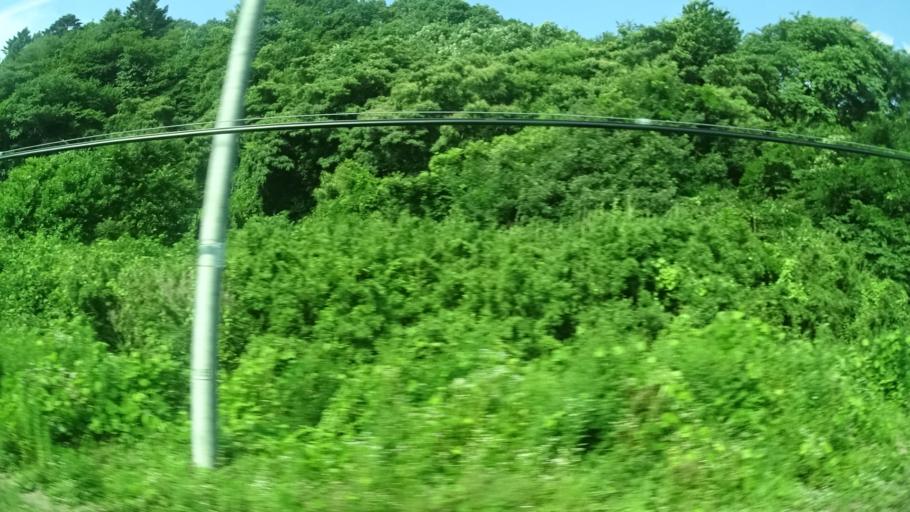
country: JP
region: Fukushima
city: Namie
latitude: 37.2914
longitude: 140.9973
